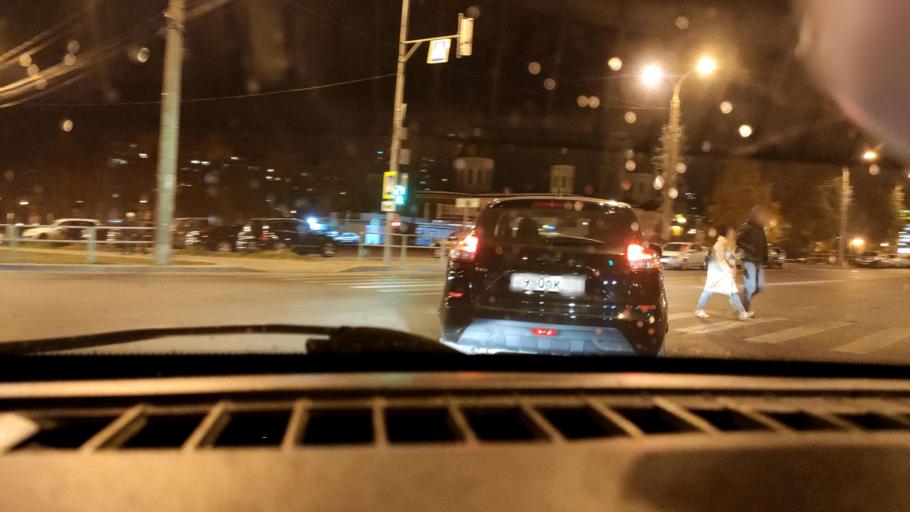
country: RU
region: Samara
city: Samara
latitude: 53.2606
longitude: 50.2079
